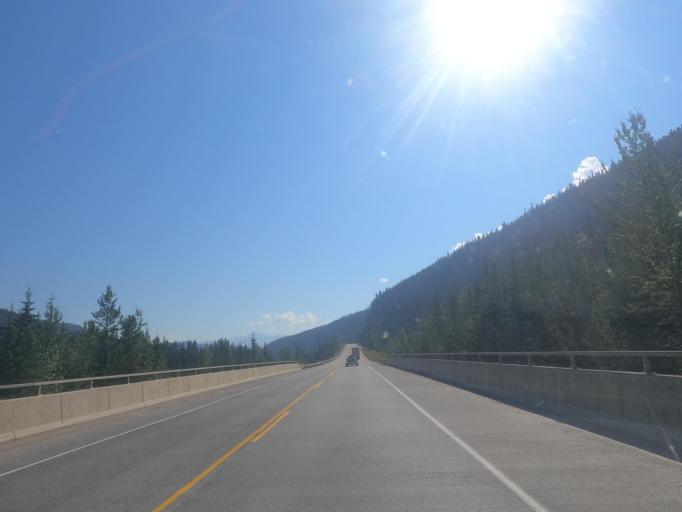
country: CA
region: Alberta
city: Jasper Park Lodge
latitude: 52.8756
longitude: -118.3149
